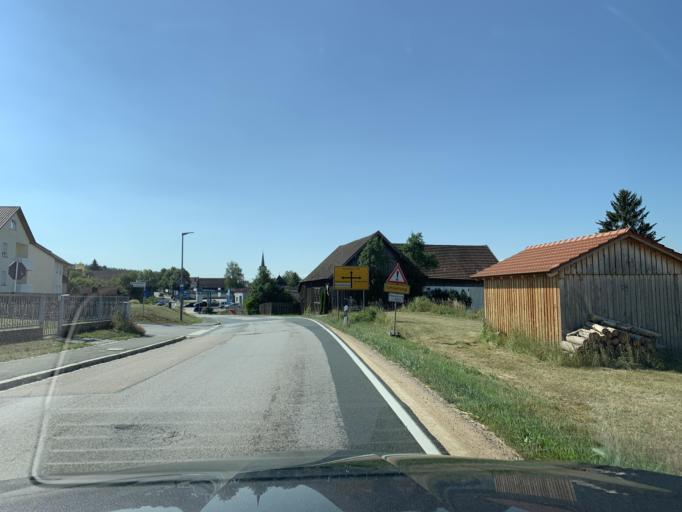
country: DE
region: Bavaria
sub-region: Upper Palatinate
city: Schwarzhofen
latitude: 49.3815
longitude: 12.3407
